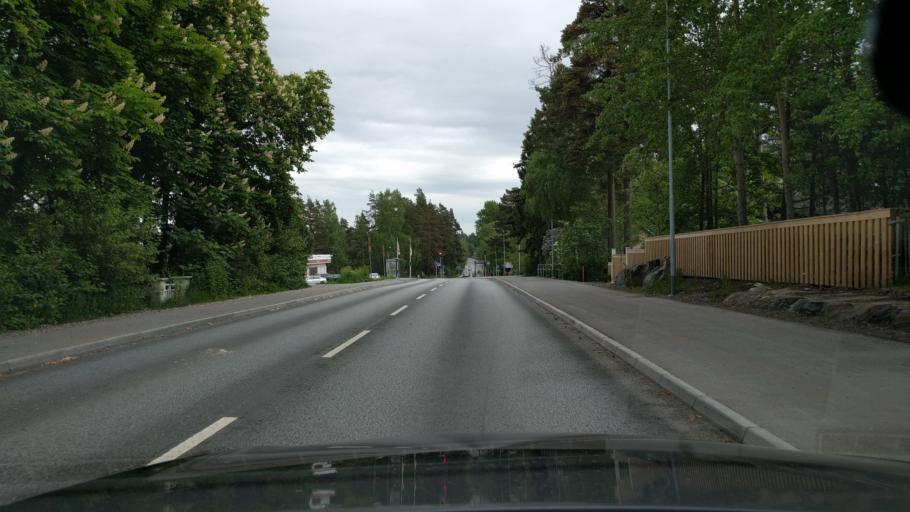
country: SE
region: Stockholm
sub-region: Taby Kommun
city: Taby
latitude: 59.4529
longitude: 18.0478
